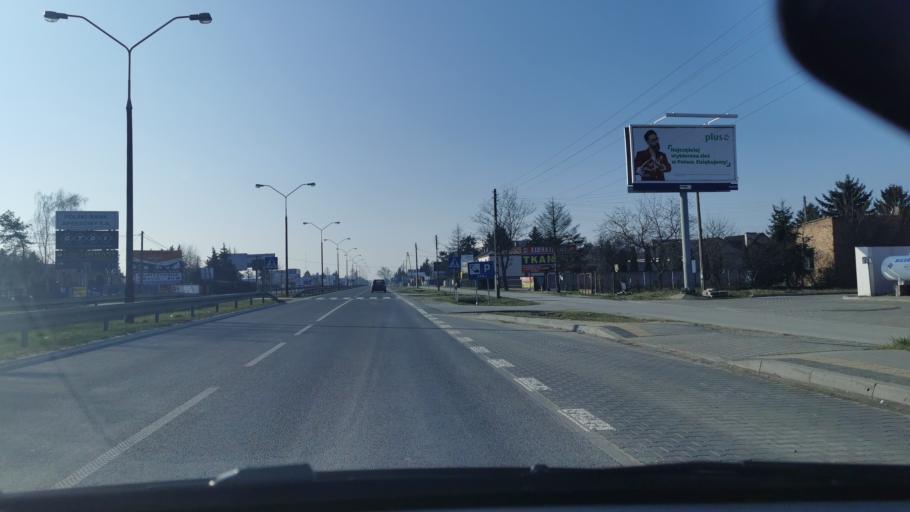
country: PL
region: Masovian Voivodeship
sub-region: Powiat pruszkowski
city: Nowe Grocholice
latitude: 52.1297
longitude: 20.8969
